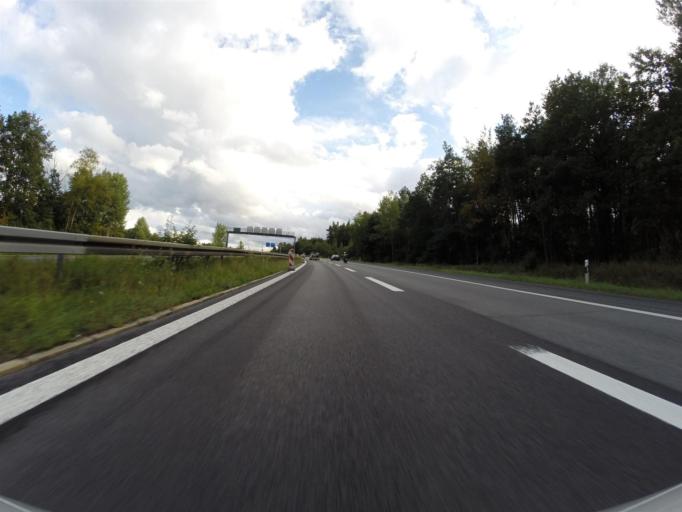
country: DE
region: Bavaria
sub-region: Regierungsbezirk Mittelfranken
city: Feucht
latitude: 49.3542
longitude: 11.2001
